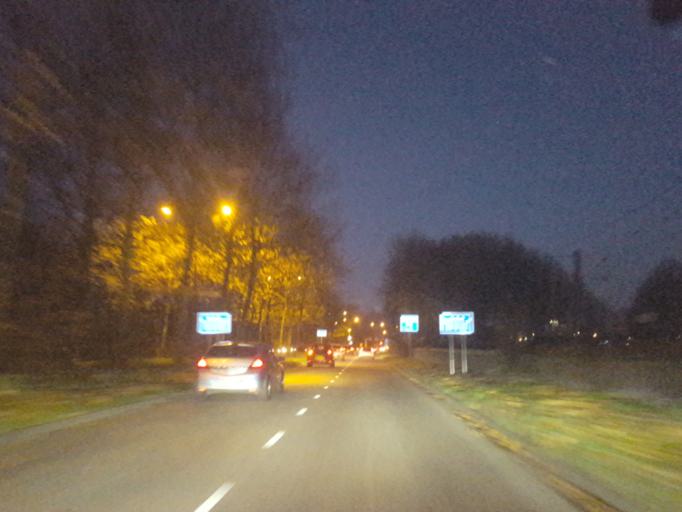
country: NL
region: Utrecht
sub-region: Gemeente Nieuwegein
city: Nieuwegein
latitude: 52.0443
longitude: 5.0822
